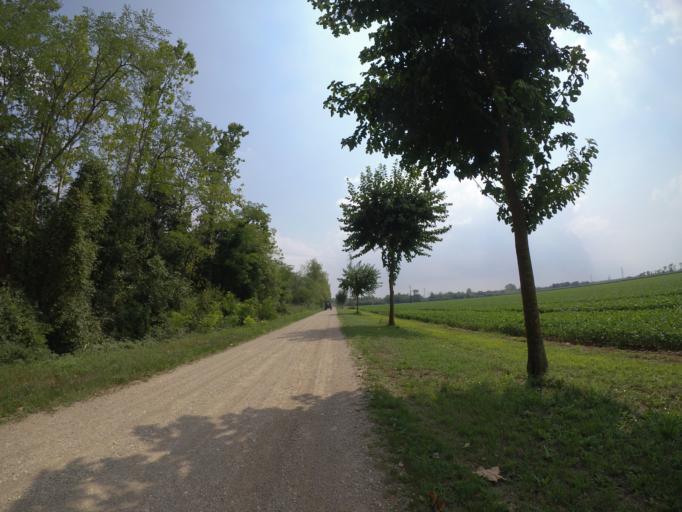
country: IT
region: Friuli Venezia Giulia
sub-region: Provincia di Udine
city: Codroipo
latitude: 45.9814
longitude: 13.0110
